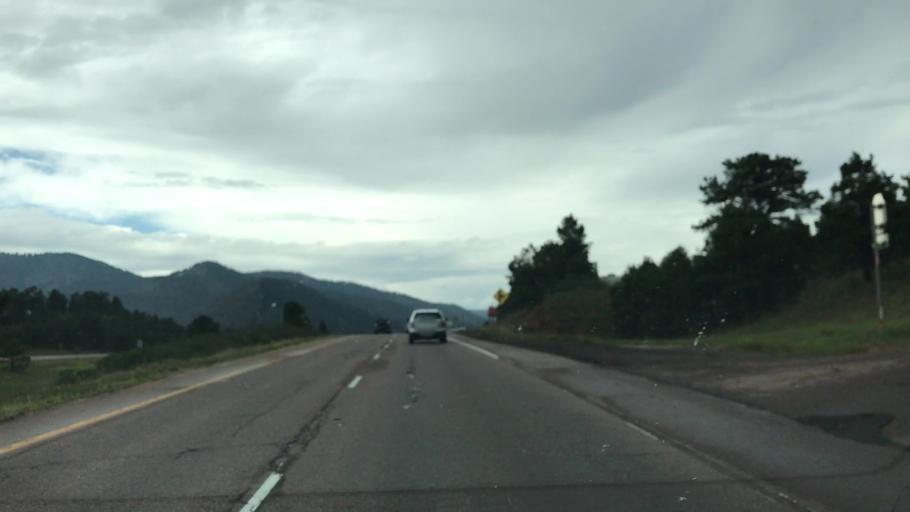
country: US
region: Colorado
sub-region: El Paso County
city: Cascade-Chipita Park
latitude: 38.9341
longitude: -105.0051
